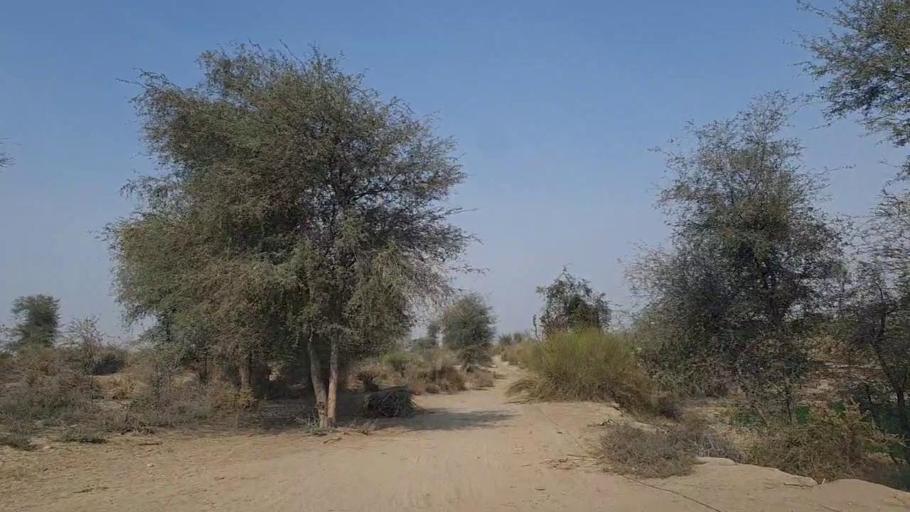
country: PK
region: Sindh
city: Daur
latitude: 26.5198
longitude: 68.4828
